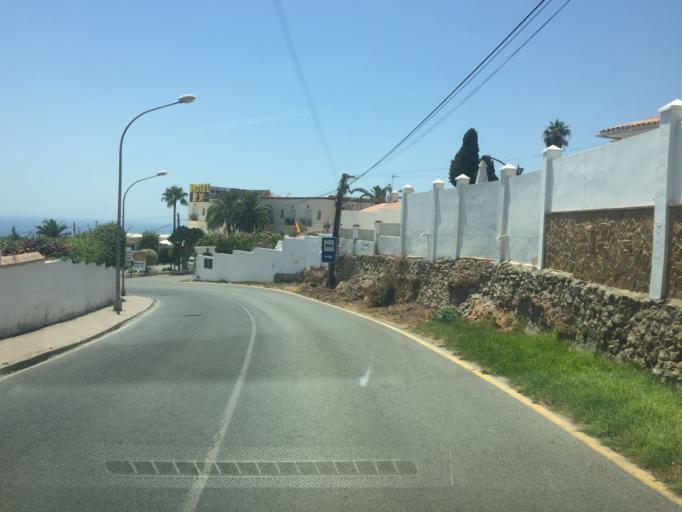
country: ES
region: Andalusia
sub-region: Provincia de Malaga
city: Nerja
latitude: 36.7614
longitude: -3.8480
